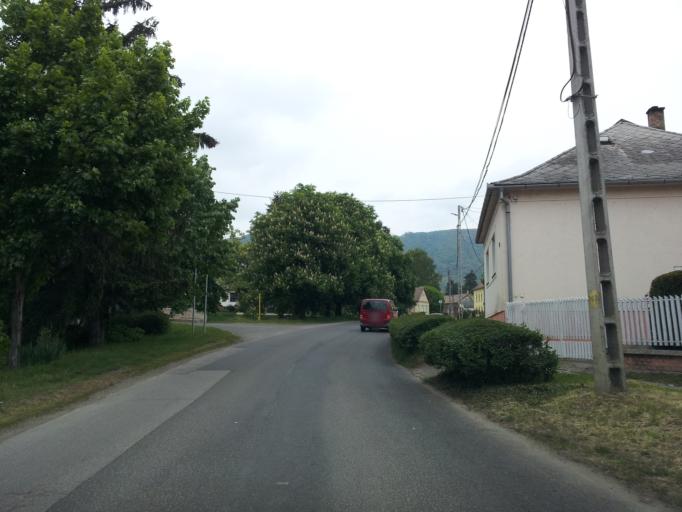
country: HU
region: Baranya
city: Hosszuheteny
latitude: 46.1611
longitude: 18.3539
